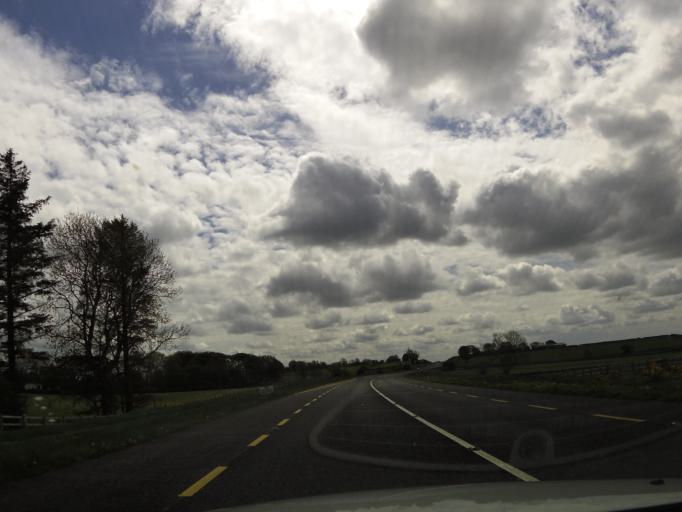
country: IE
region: Connaught
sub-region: County Galway
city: Tuam
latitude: 53.5682
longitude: -8.8398
